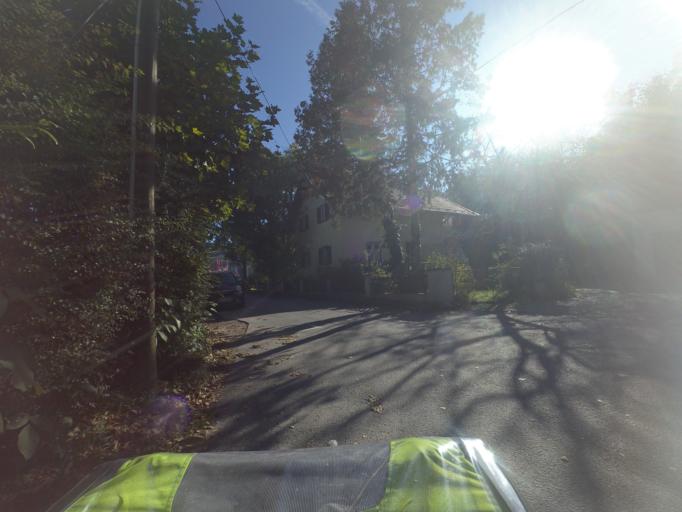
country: AT
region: Salzburg
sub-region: Politischer Bezirk Salzburg-Umgebung
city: Anif
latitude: 47.7711
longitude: 13.0683
